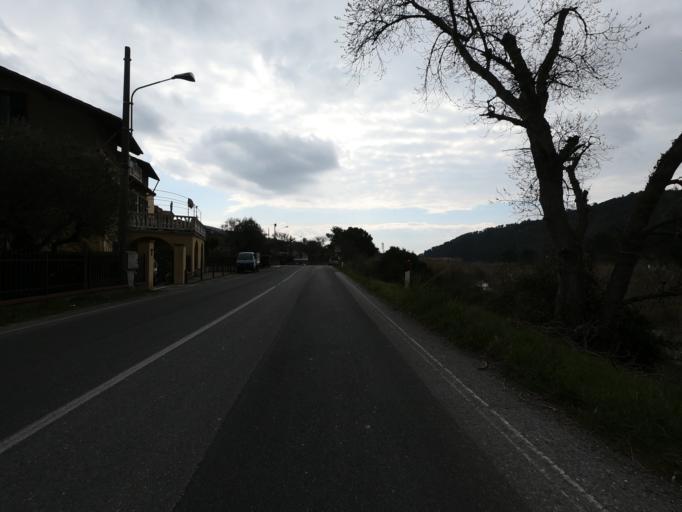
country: IT
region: Liguria
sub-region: Provincia di Imperia
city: Villa Faraldi
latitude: 43.9923
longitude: 8.1207
